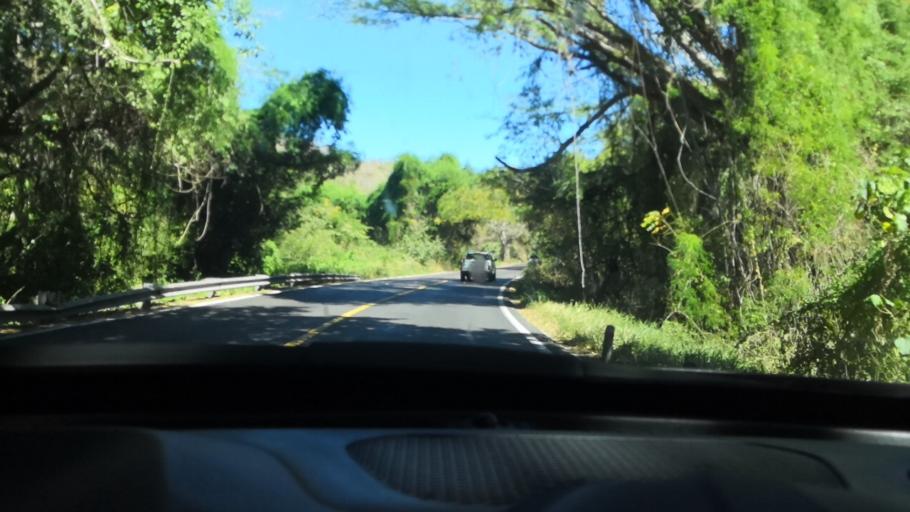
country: MX
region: Nayarit
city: Bucerias
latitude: 20.7819
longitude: -105.3874
